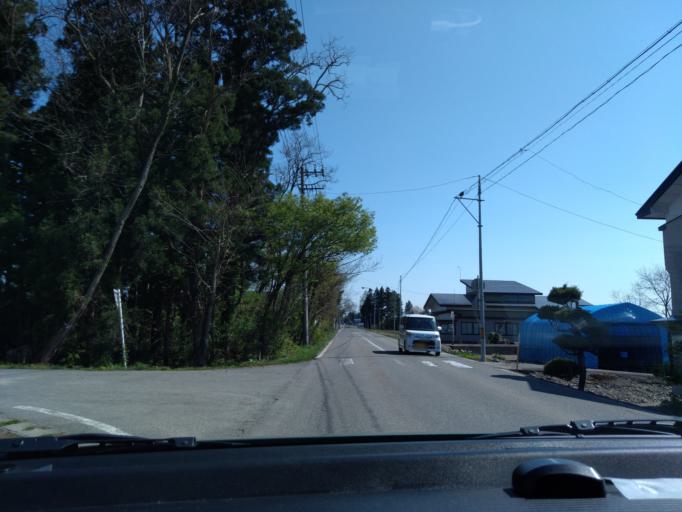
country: JP
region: Akita
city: Kakunodatemachi
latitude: 39.5391
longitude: 140.5852
